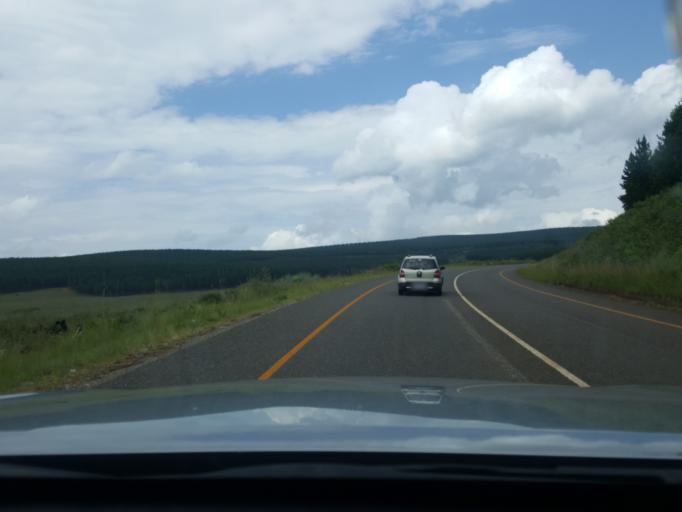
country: ZA
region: Mpumalanga
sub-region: Ehlanzeni District
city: Graksop
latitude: -25.1310
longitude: 30.8153
